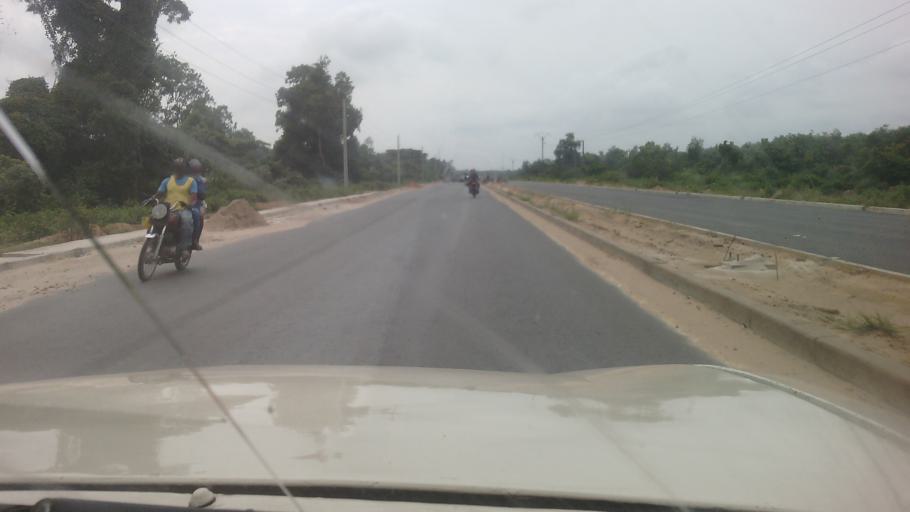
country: BJ
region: Atlantique
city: Ouidah
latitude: 6.3776
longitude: 2.1580
